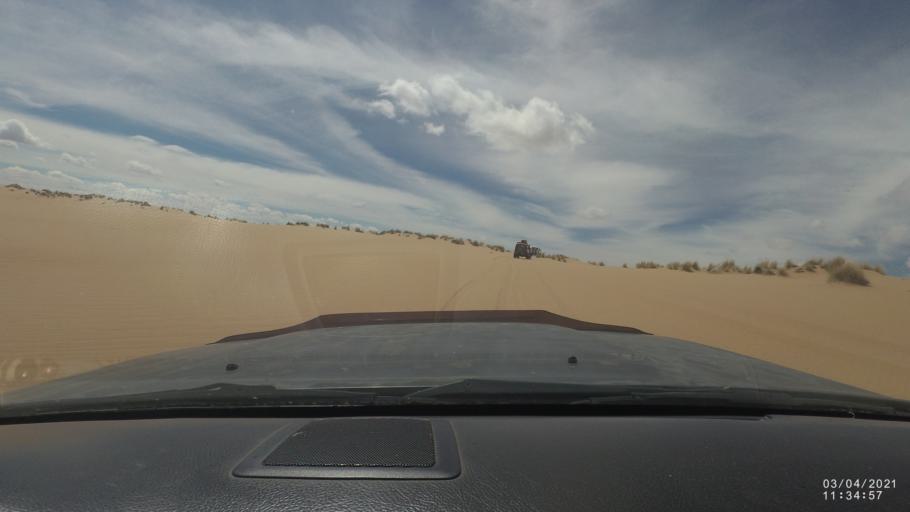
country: BO
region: Oruro
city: Poopo
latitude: -18.7012
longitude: -67.5047
